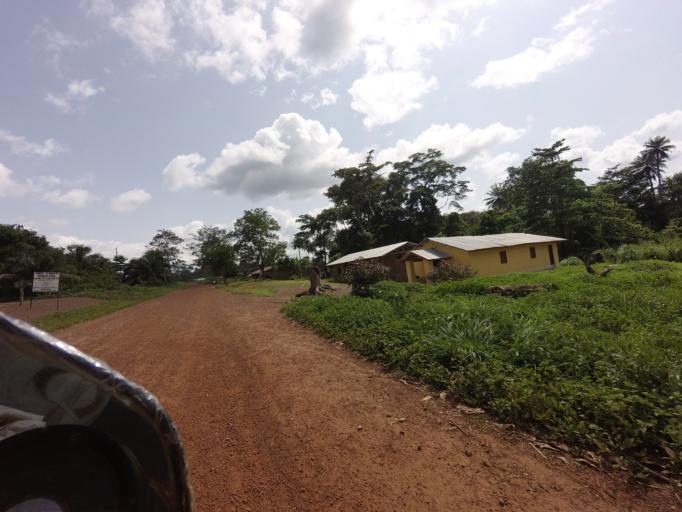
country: SL
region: Eastern Province
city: Bunumbu
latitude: 8.0891
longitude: -10.8116
